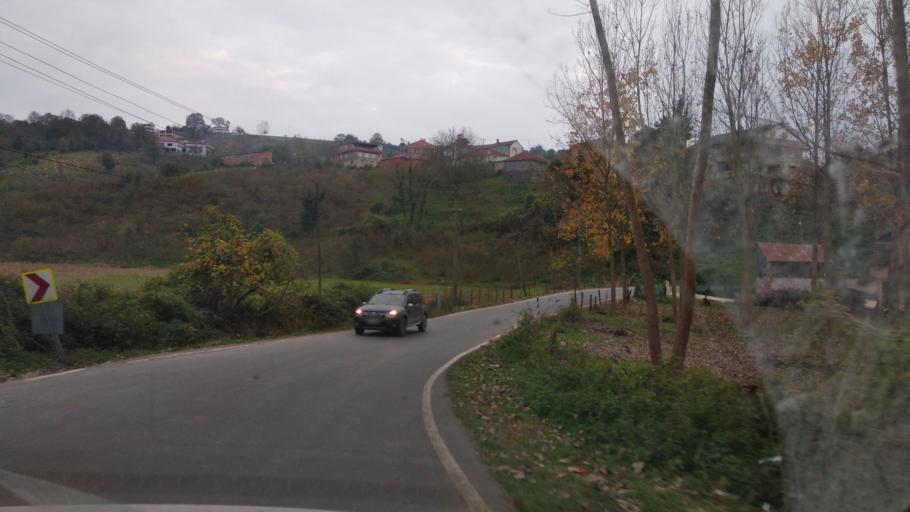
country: TR
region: Sakarya
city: Ortakoy
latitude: 41.0375
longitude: 30.6475
